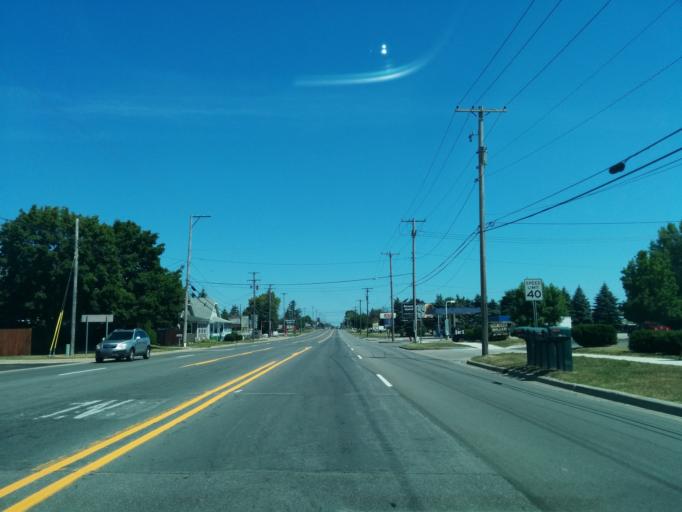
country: US
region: Michigan
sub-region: Bay County
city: Bay City
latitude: 43.5809
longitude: -83.9157
